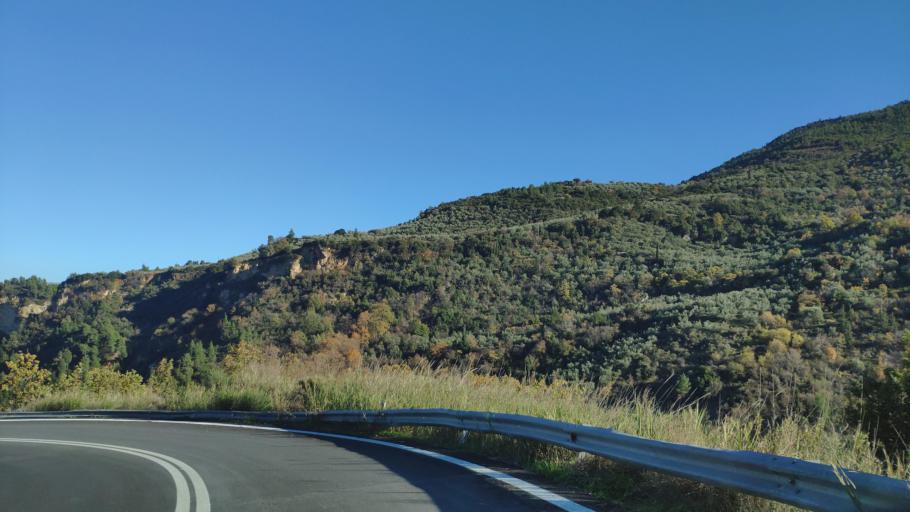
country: GR
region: Peloponnese
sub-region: Nomos Korinthias
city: Xylokastro
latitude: 38.0006
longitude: 22.5053
